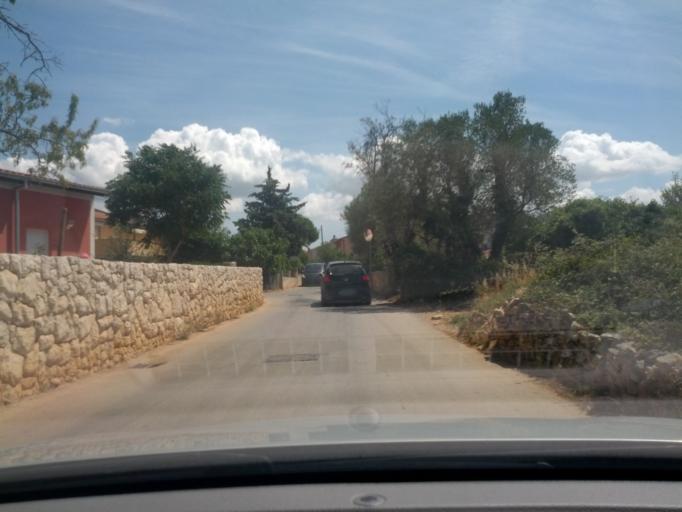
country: HR
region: Istarska
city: Fazana
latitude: 44.9527
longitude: 13.7938
